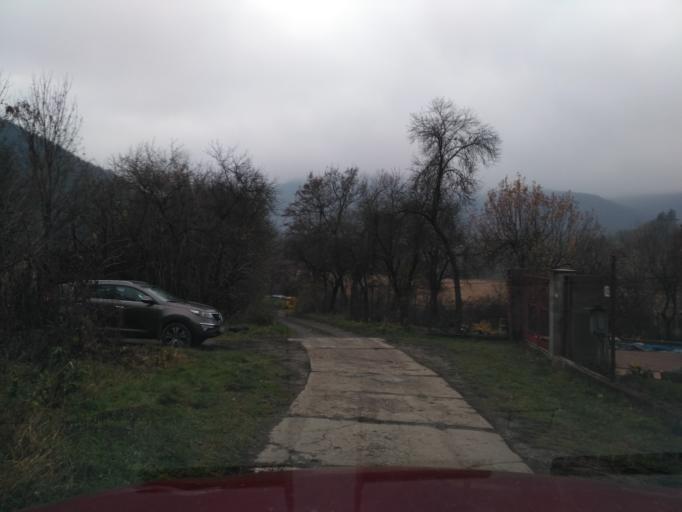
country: SK
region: Kosicky
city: Kosice
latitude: 48.8471
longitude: 21.2314
